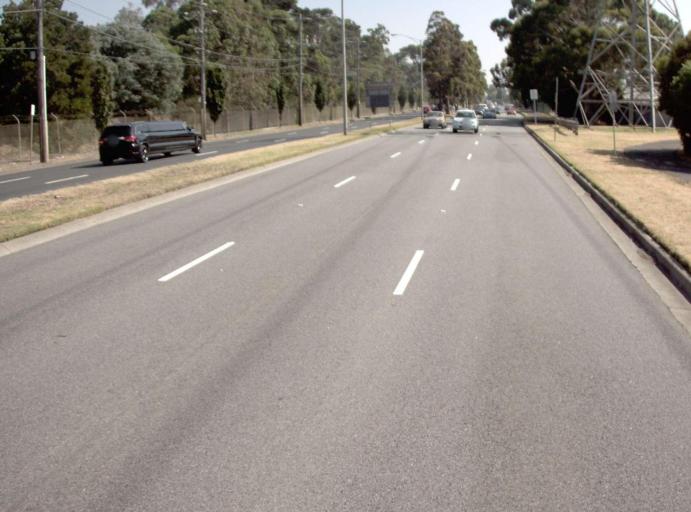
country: AU
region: Victoria
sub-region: Monash
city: Oakleigh South
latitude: -37.9363
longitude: 145.0802
